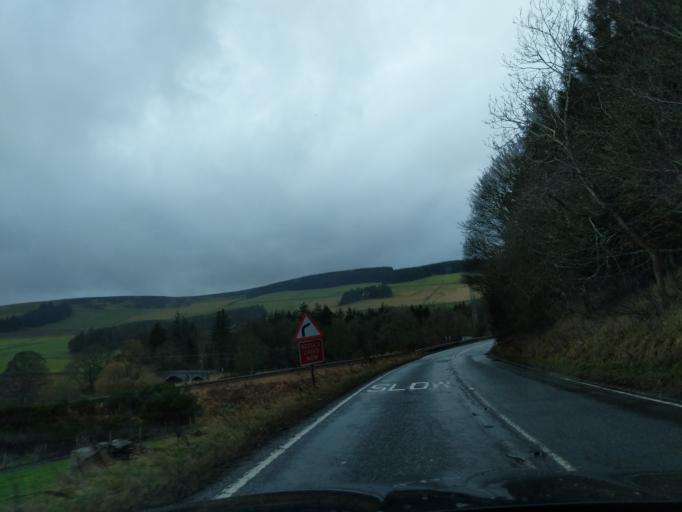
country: GB
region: Scotland
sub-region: The Scottish Borders
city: Galashiels
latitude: 55.6648
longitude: -2.8756
